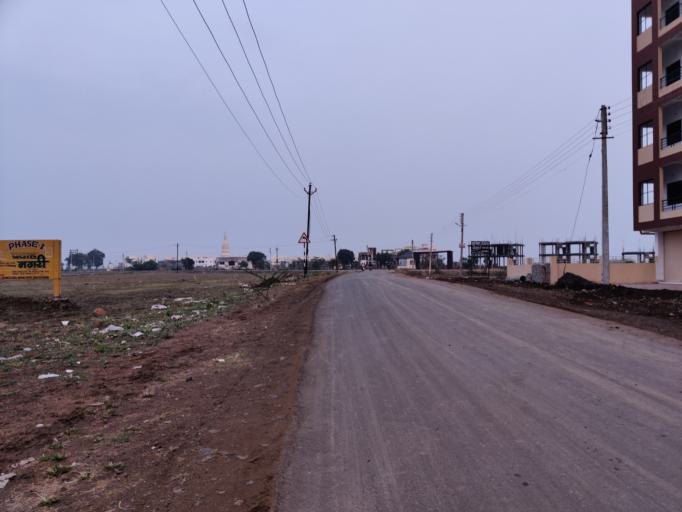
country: IN
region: Maharashtra
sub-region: Nagpur Division
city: Kamthi
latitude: 21.1959
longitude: 79.1519
